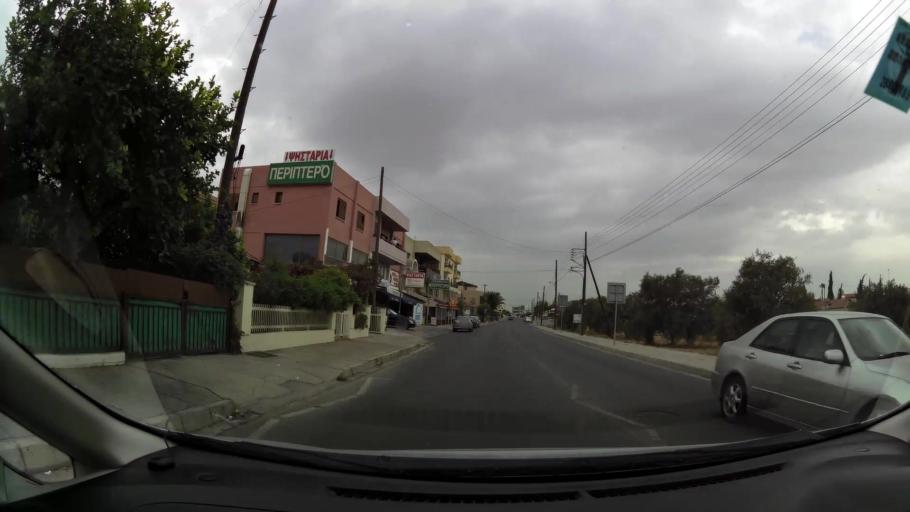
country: CY
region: Lefkosia
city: Geri
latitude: 35.1046
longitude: 33.3889
